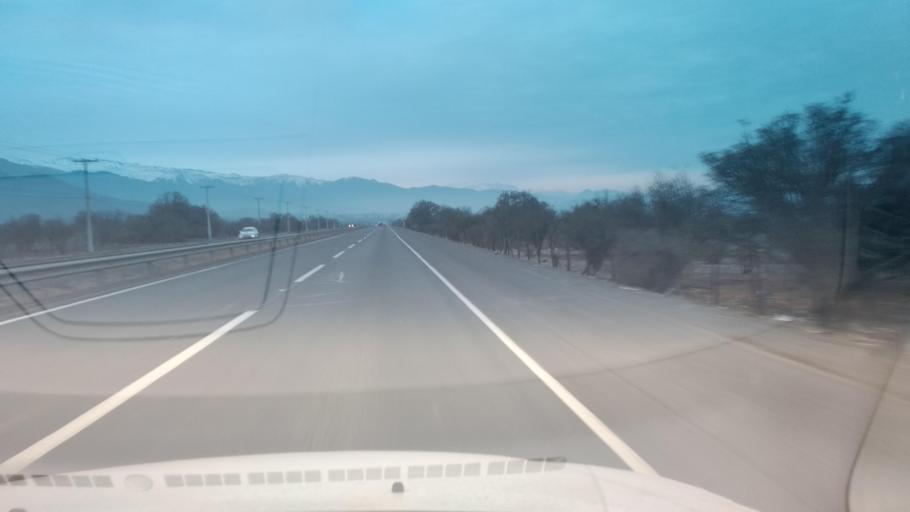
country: CL
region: Santiago Metropolitan
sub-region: Provincia de Chacabuco
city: Chicureo Abajo
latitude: -33.1111
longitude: -70.6874
